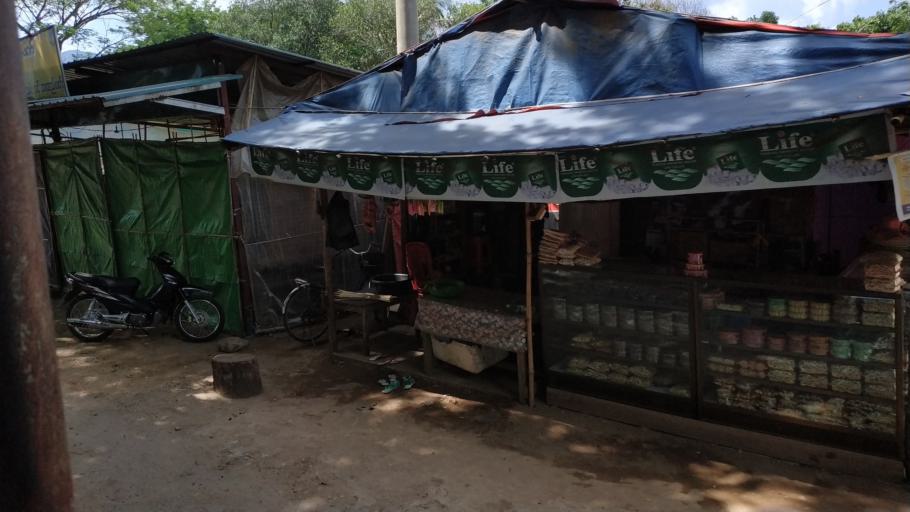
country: MM
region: Mon
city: Kyaikto
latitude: 17.4008
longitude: 97.0767
